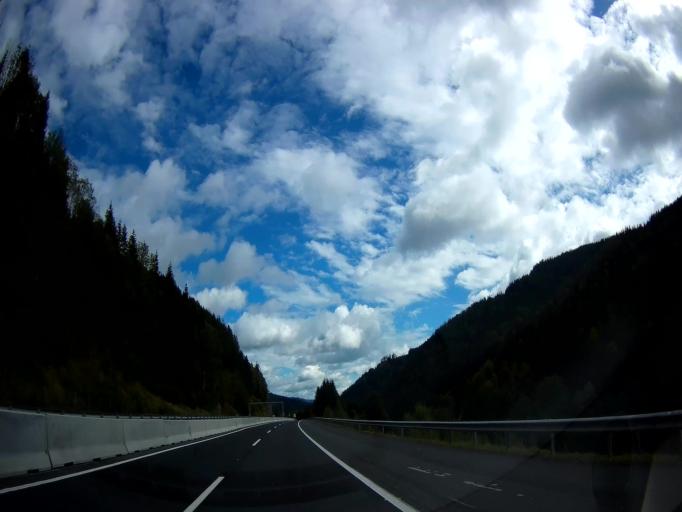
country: AT
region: Styria
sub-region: Politischer Bezirk Graz-Umgebung
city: Ubelbach
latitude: 47.2464
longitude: 15.1615
